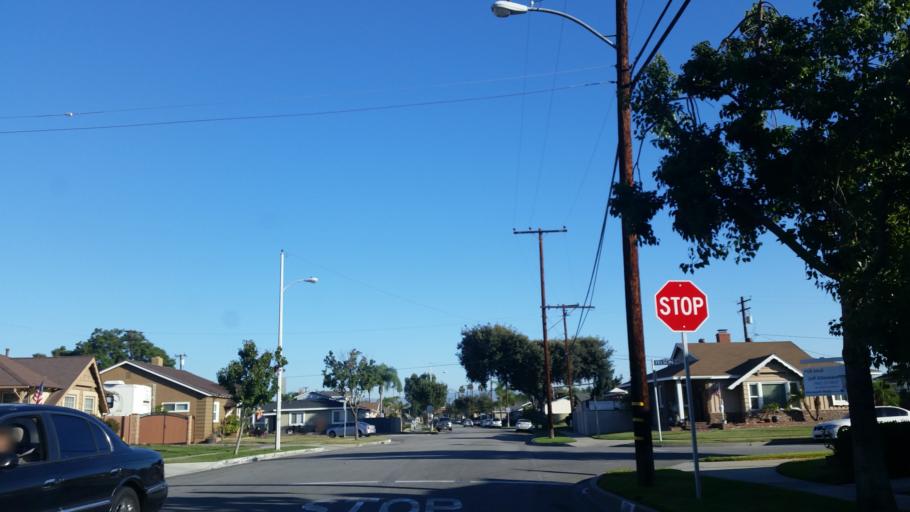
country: US
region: California
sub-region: Los Angeles County
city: Bellflower
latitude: 33.8686
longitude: -118.1114
